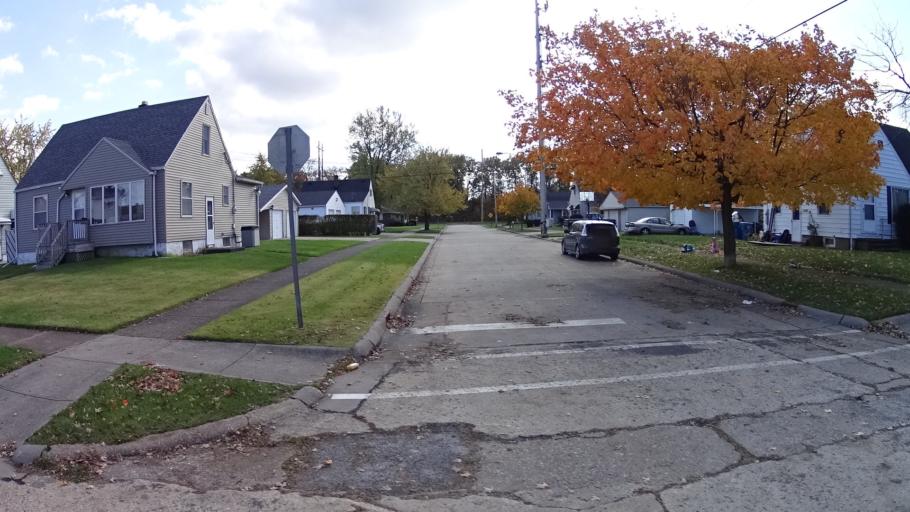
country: US
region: Ohio
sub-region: Lorain County
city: Sheffield
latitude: 41.4399
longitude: -82.1126
